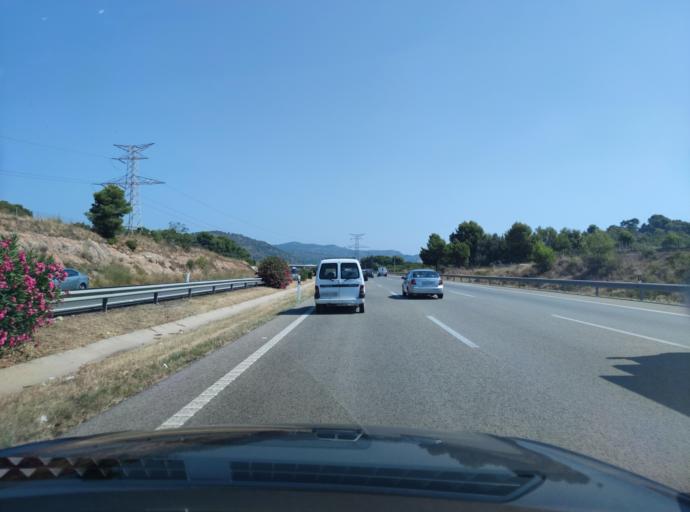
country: ES
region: Valencia
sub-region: Provincia de Valencia
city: Petres
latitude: 39.6665
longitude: -0.3027
